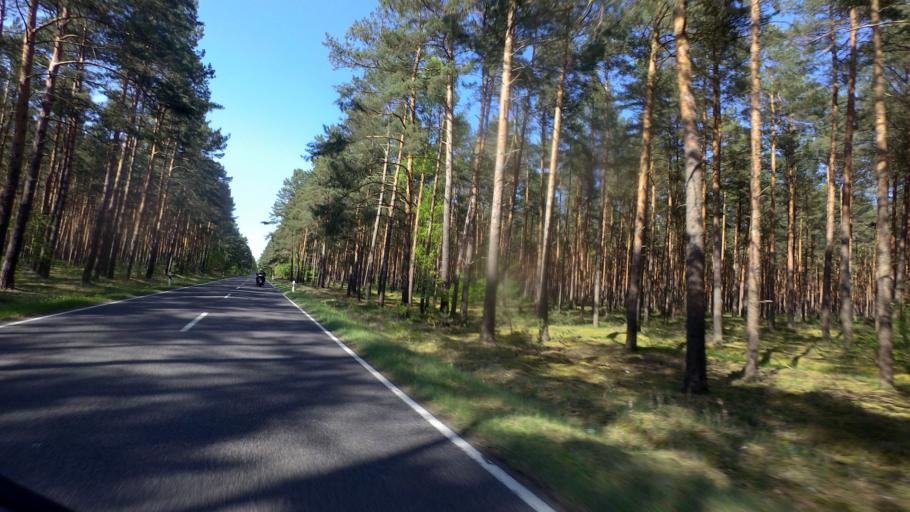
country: DE
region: Brandenburg
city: Gross Koris
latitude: 52.2070
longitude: 13.6909
